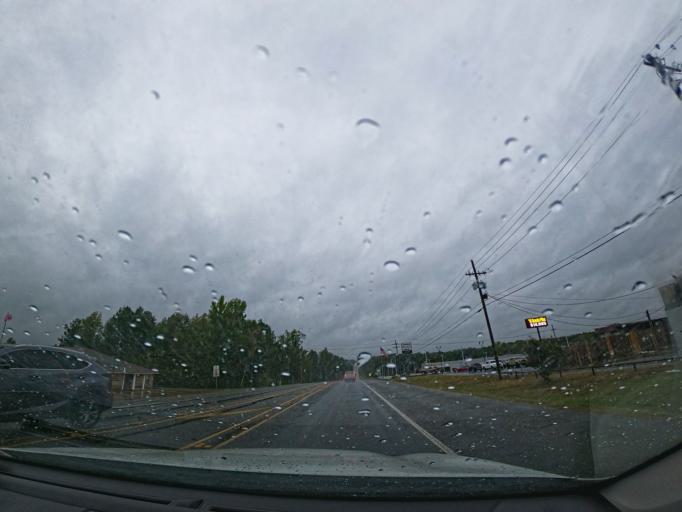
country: US
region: Louisiana
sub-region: Webster Parish
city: Minden
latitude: 32.6251
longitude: -93.2497
